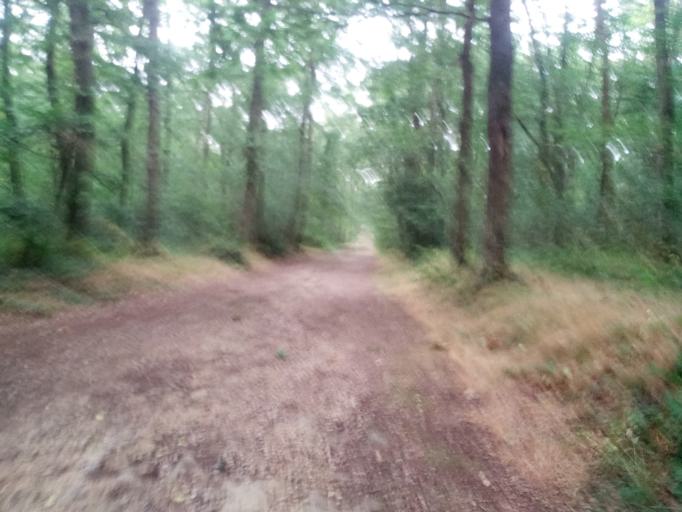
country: FR
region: Lower Normandy
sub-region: Departement du Calvados
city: Clinchamps-sur-Orne
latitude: 49.0456
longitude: -0.4314
